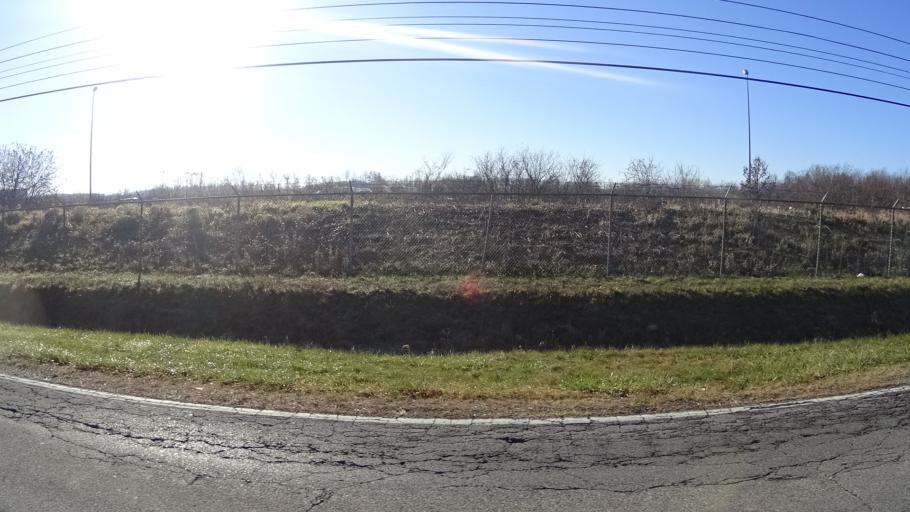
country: US
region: Ohio
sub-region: Lorain County
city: Sheffield Lake
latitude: 41.4823
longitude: -82.0831
